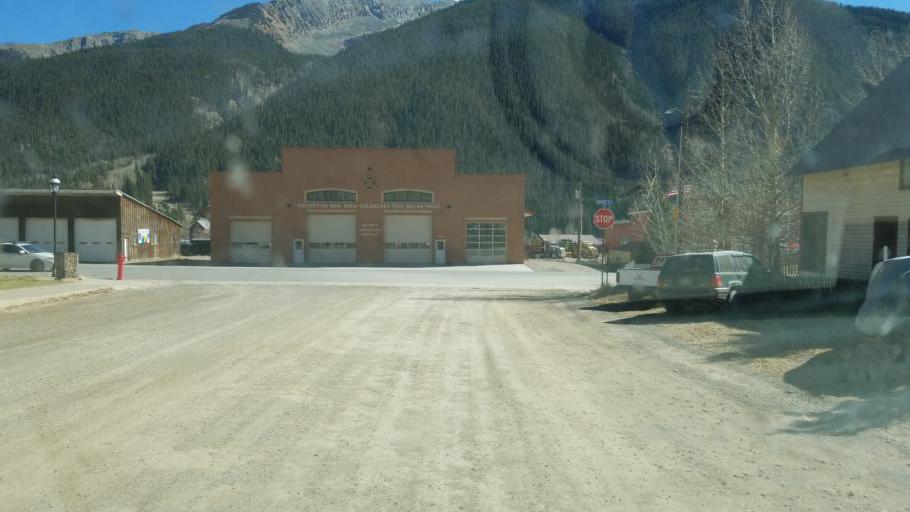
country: US
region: Colorado
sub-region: San Juan County
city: Silverton
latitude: 37.8144
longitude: -107.6625
